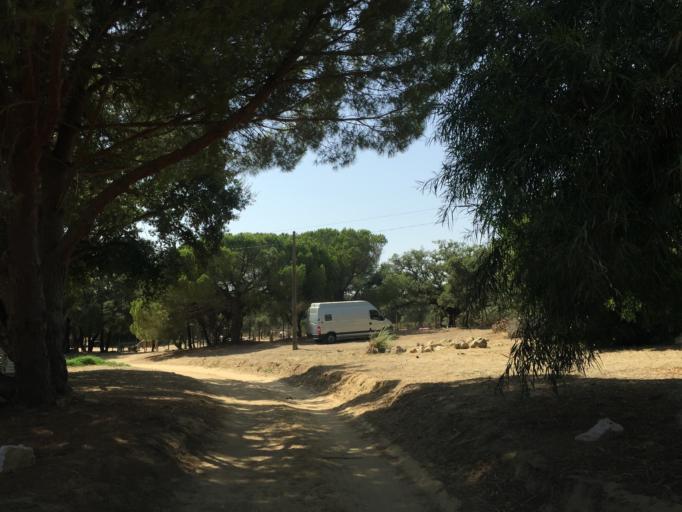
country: PT
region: Faro
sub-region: Albufeira
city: Ferreiras
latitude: 37.1035
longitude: -8.2029
